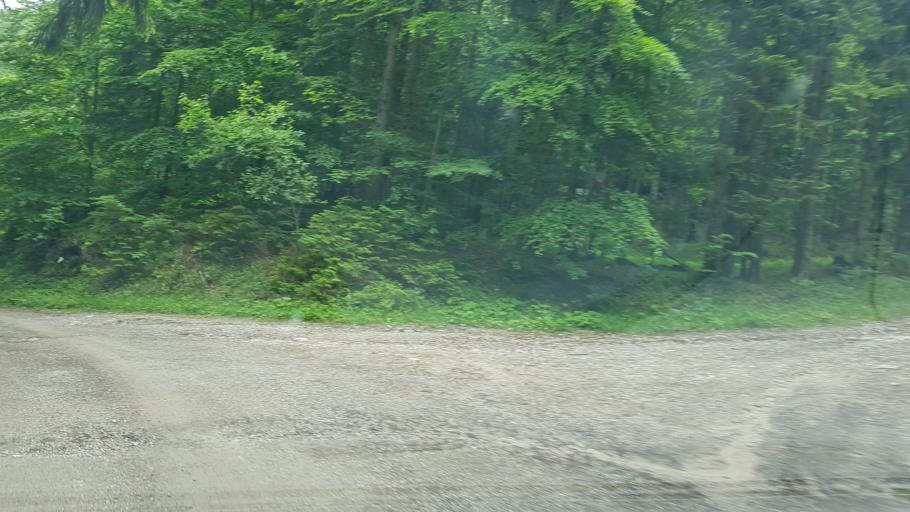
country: SI
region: Dobrna
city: Dobrna
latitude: 46.3822
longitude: 15.2275
